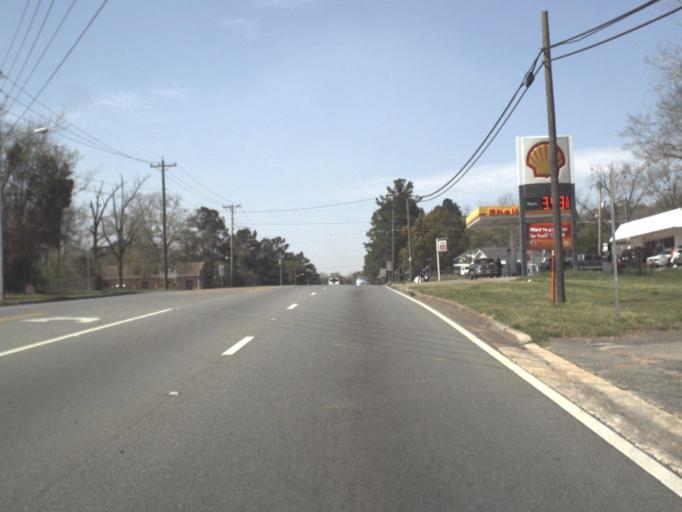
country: US
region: Florida
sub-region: Gadsden County
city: Quincy
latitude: 30.5828
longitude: -84.5631
